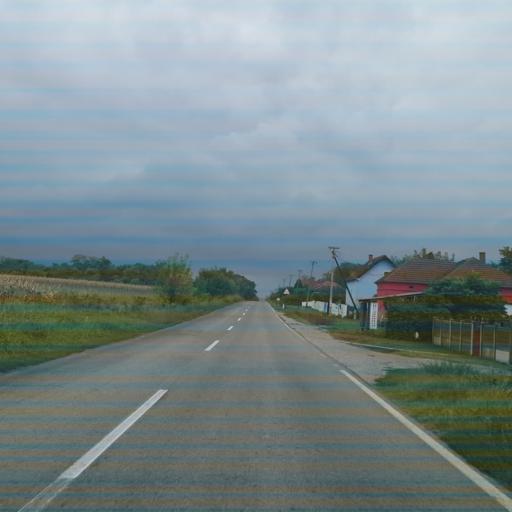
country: RS
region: Central Serbia
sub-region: Nisavski Okrug
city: Razanj
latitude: 43.6116
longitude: 21.5942
